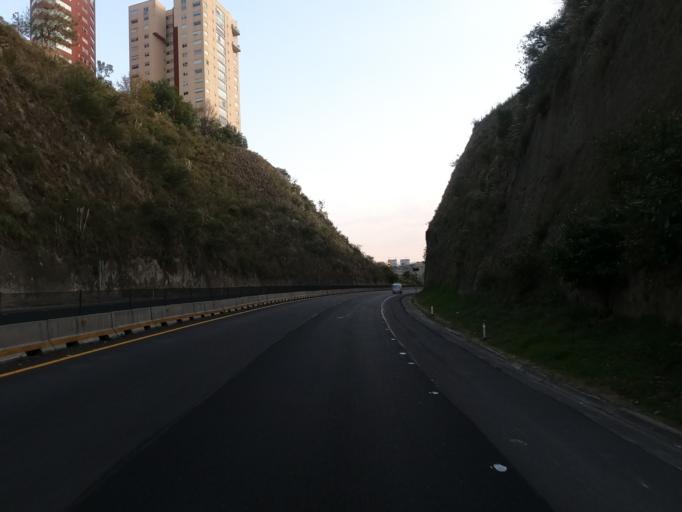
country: MX
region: Mexico
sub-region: Naucalpan de Juarez
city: Ejido el Castillo
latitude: 19.4278
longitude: -99.2952
